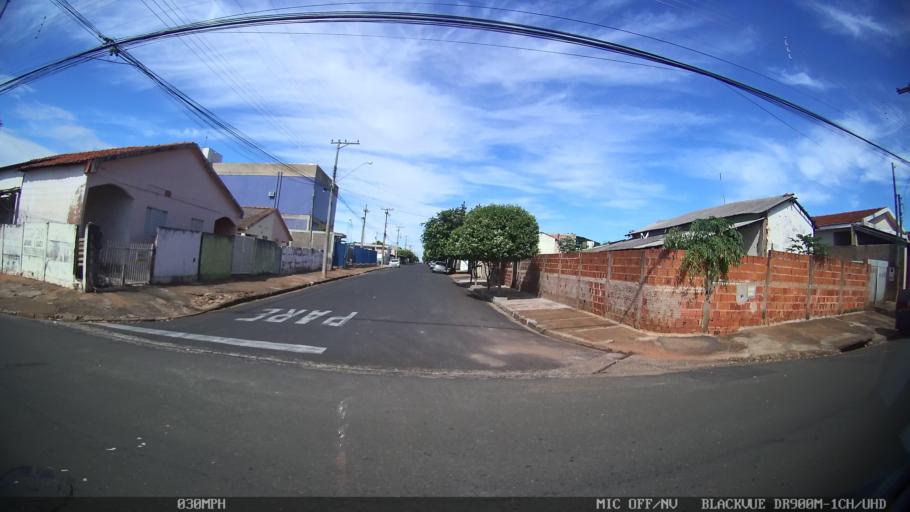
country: BR
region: Sao Paulo
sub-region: Sao Jose Do Rio Preto
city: Sao Jose do Rio Preto
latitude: -20.8430
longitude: -49.3443
